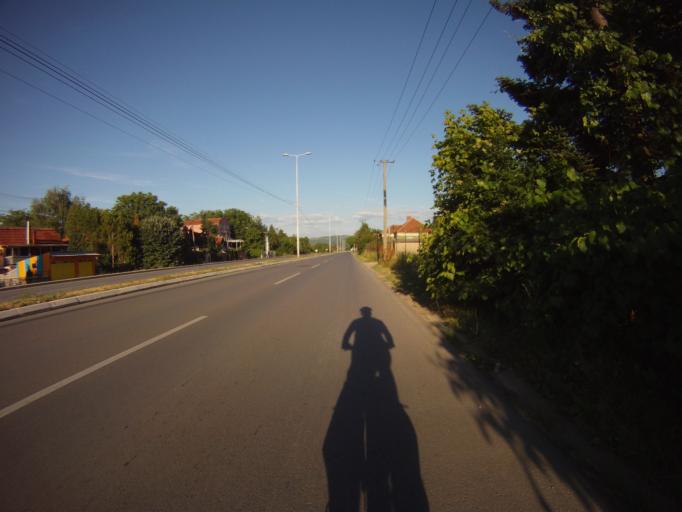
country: RS
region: Central Serbia
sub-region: Nisavski Okrug
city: Niska Banja
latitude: 43.3015
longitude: 21.9884
